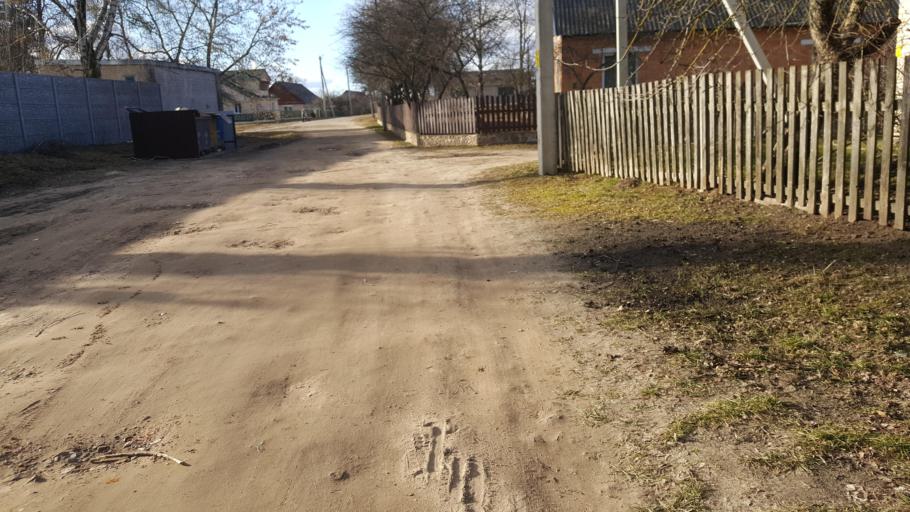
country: BY
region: Brest
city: Kamyanyets
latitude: 52.3919
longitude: 23.8321
